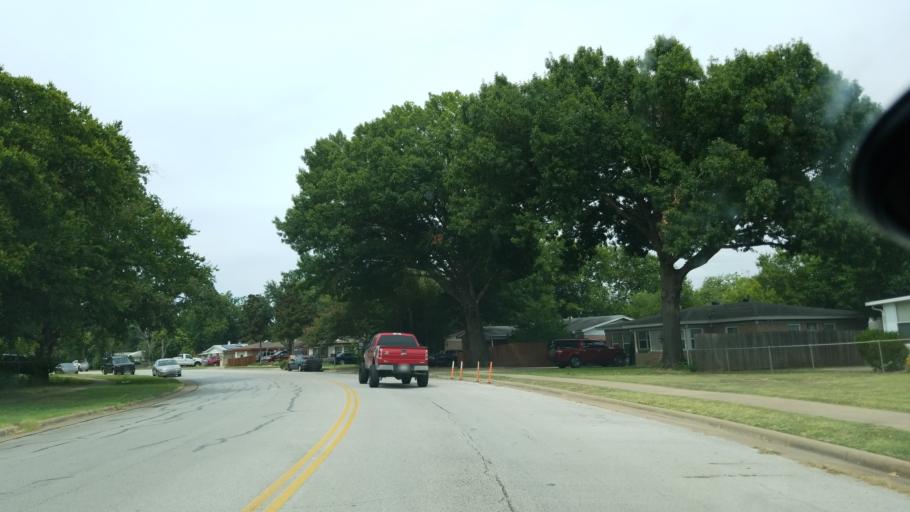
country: US
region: Texas
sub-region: Tarrant County
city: Arlington
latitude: 32.7175
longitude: -97.0838
